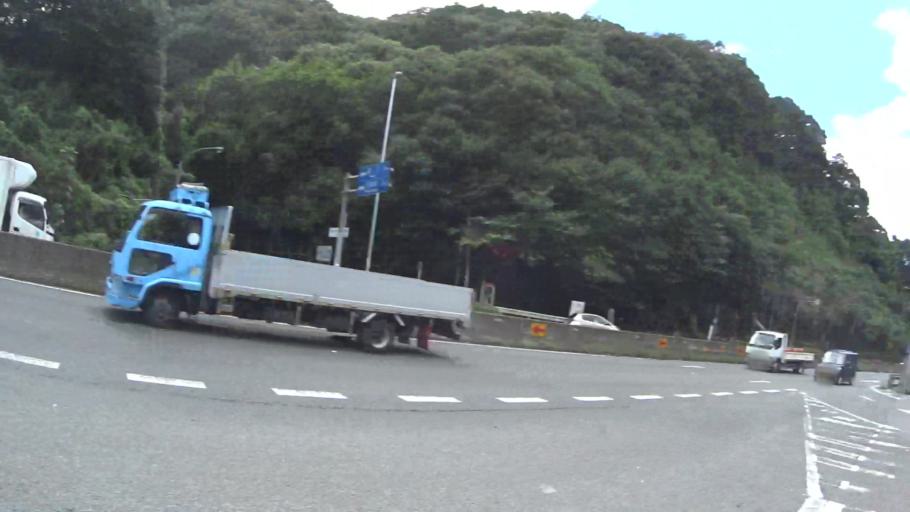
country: JP
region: Kyoto
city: Kyoto
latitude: 34.9892
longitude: 135.7876
